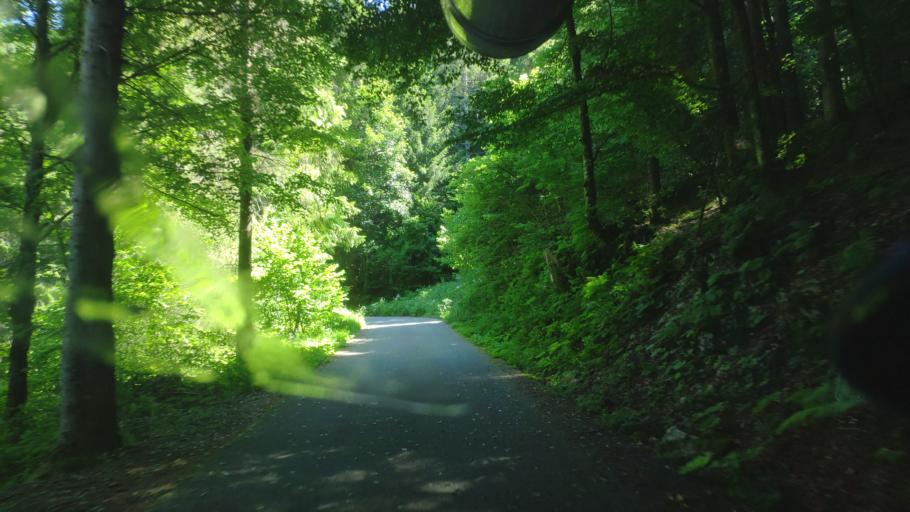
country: IT
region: Veneto
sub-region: Provincia di Vicenza
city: Cogollo del Cengio
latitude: 45.8210
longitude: 11.4401
